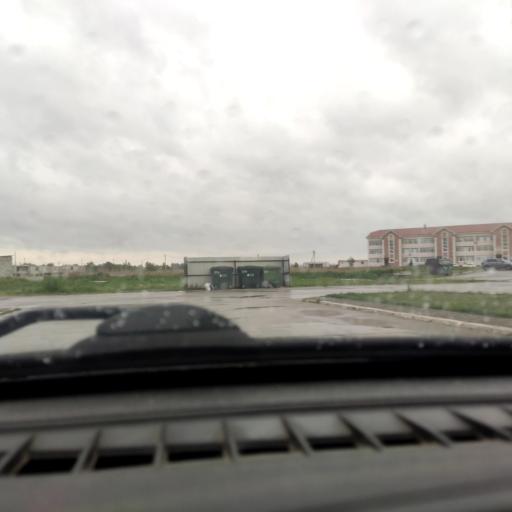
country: RU
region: Samara
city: Podstepki
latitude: 53.5292
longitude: 49.1801
